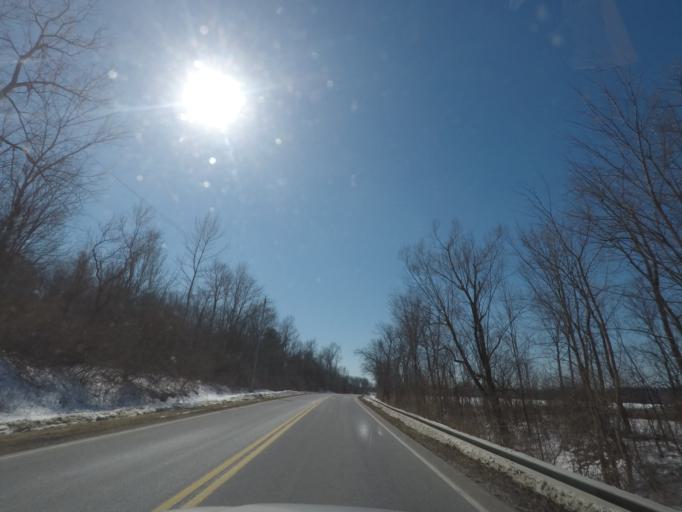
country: US
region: New York
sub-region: Saratoga County
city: Stillwater
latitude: 42.9673
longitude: -73.6196
